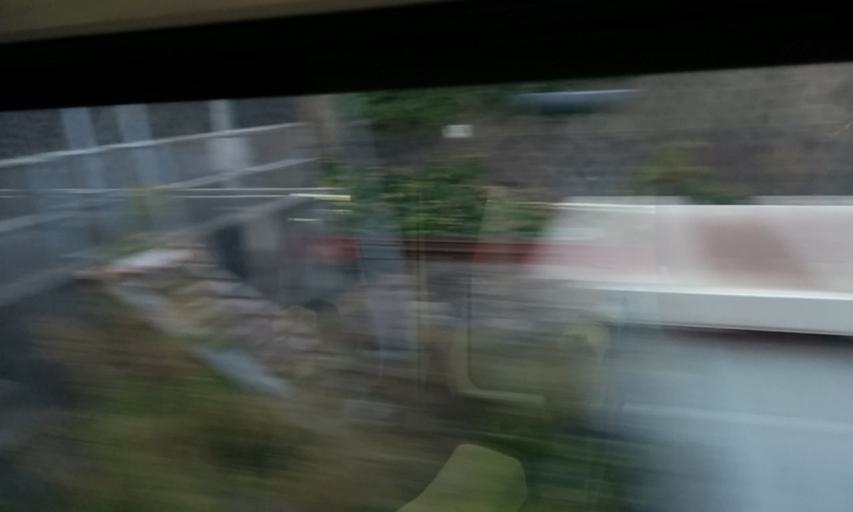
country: JP
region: Aichi
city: Nagoya-shi
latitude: 35.1430
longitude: 136.9018
